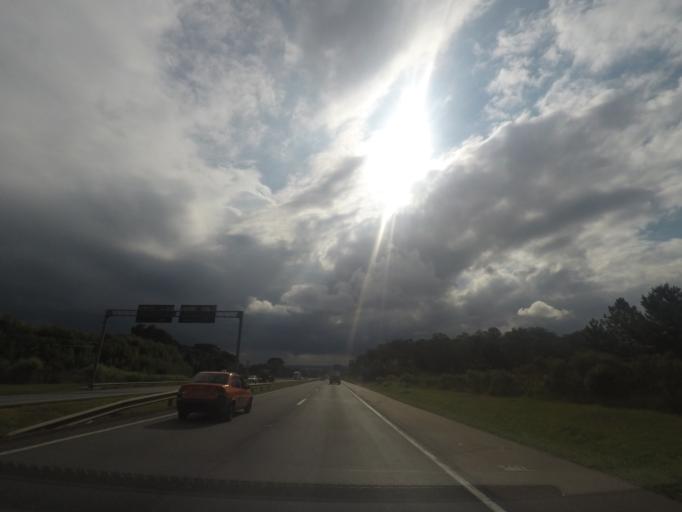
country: BR
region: Parana
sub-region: Sao Jose Dos Pinhais
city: Sao Jose dos Pinhais
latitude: -25.5041
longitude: -49.1443
